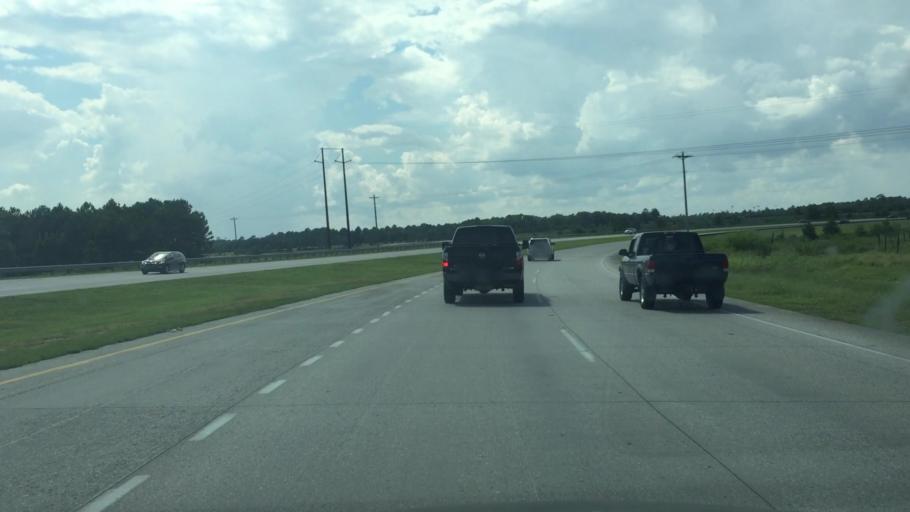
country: US
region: South Carolina
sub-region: Horry County
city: North Myrtle Beach
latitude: 33.8383
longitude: -78.6963
